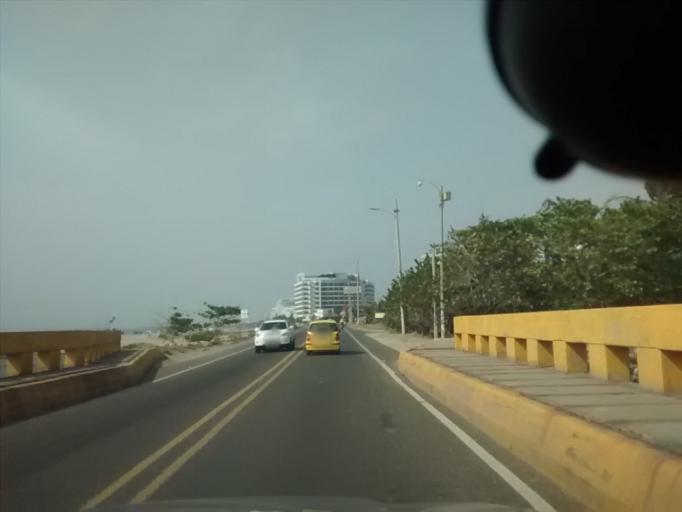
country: CO
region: Bolivar
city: Cartagena
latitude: 10.4558
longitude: -75.5112
